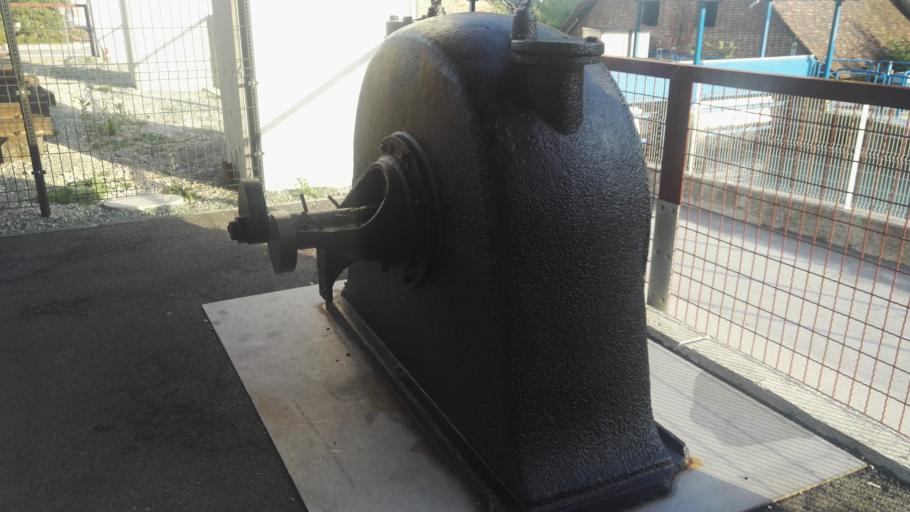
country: SI
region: Jesenice
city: Jesenice
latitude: 46.4333
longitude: 14.0565
